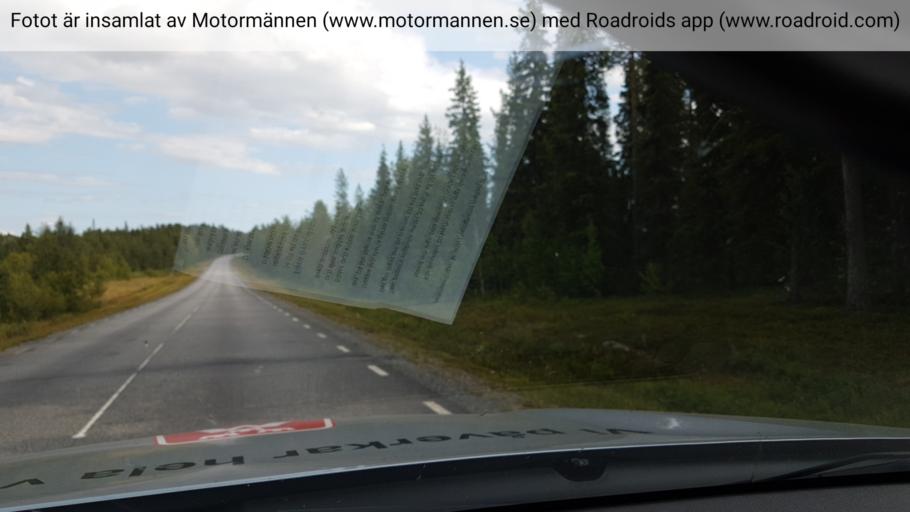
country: SE
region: Vaesterbotten
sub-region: Skelleftea Kommun
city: Storvik
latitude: 65.3370
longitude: 20.5580
